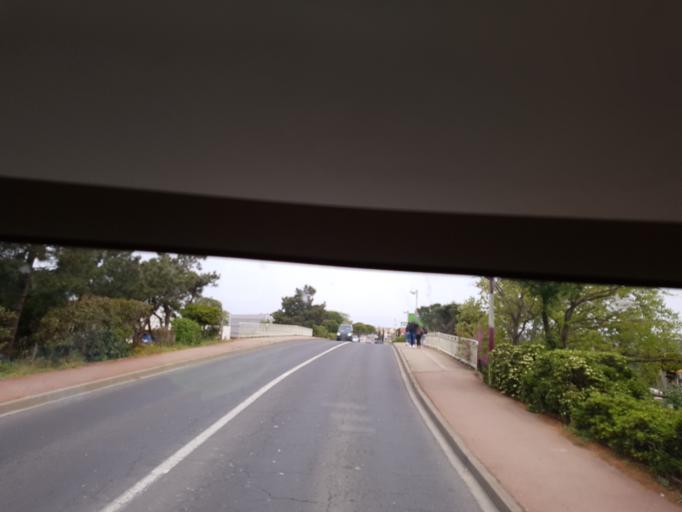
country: FR
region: Languedoc-Roussillon
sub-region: Departement de l'Aude
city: Narbonne
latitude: 43.1717
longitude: 2.9905
